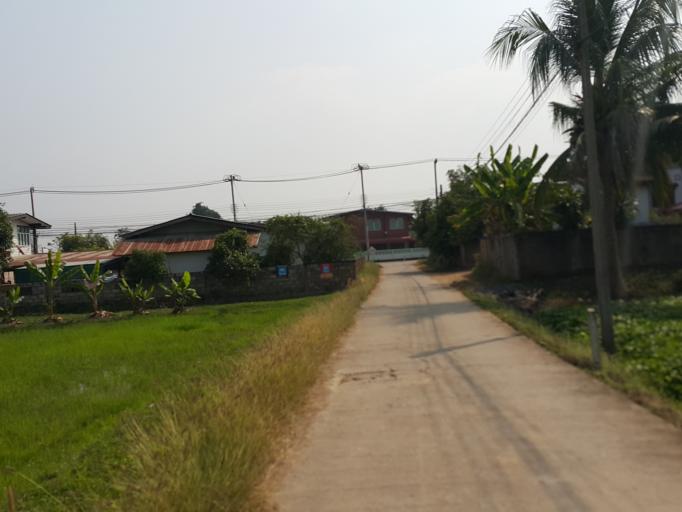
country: TH
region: Sukhothai
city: Thung Saliam
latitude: 17.3287
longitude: 99.5292
